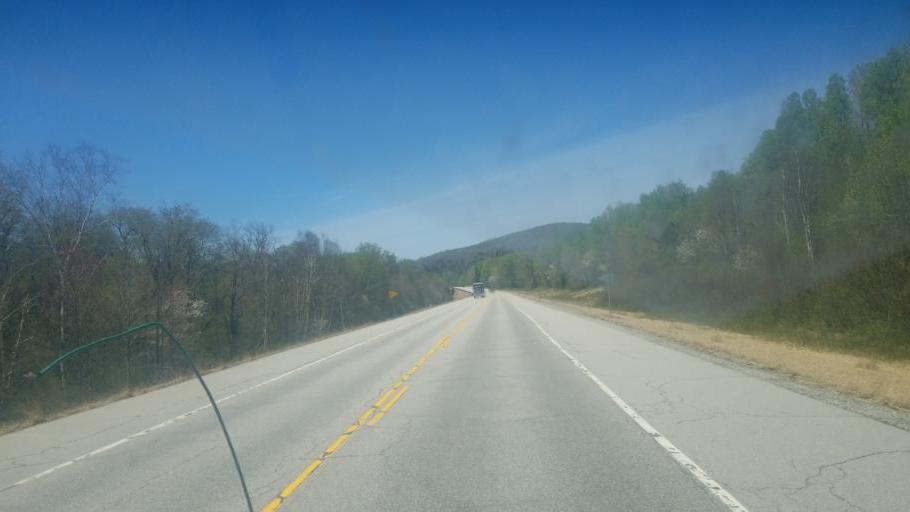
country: US
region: New Hampshire
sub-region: Grafton County
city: Deerfield
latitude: 44.2685
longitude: -71.5046
